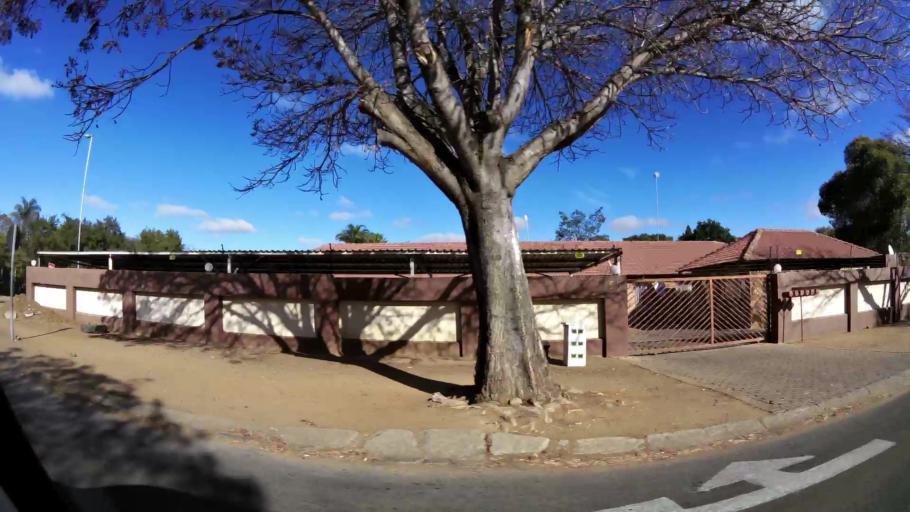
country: ZA
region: Limpopo
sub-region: Capricorn District Municipality
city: Polokwane
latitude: -23.9032
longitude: 29.4585
